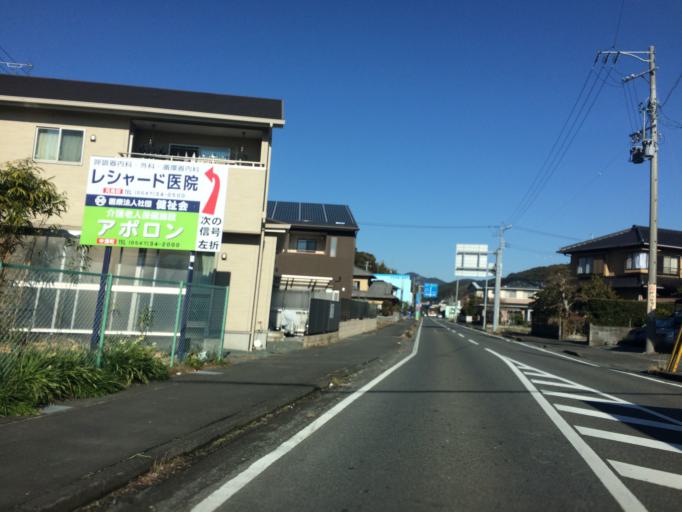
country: JP
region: Shizuoka
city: Shimada
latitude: 34.8370
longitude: 138.1999
